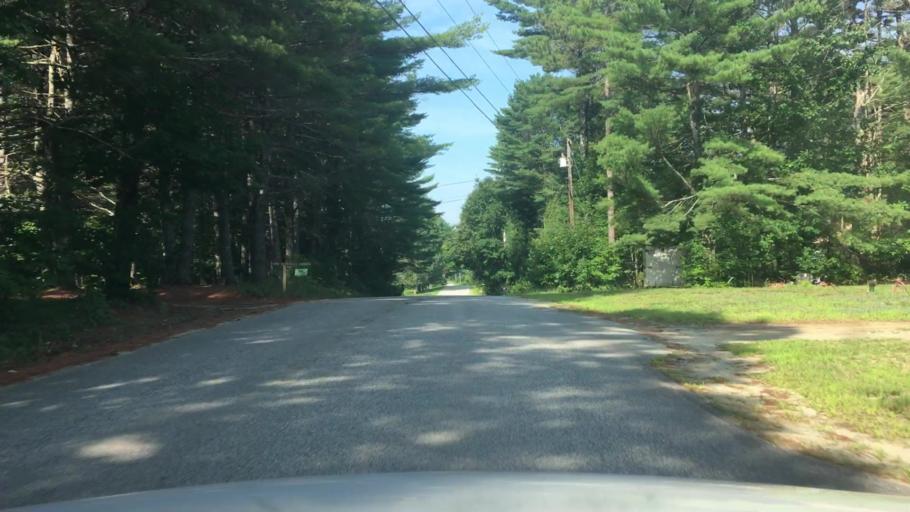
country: US
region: Maine
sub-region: Kennebec County
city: Monmouth
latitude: 44.2430
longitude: -70.0963
